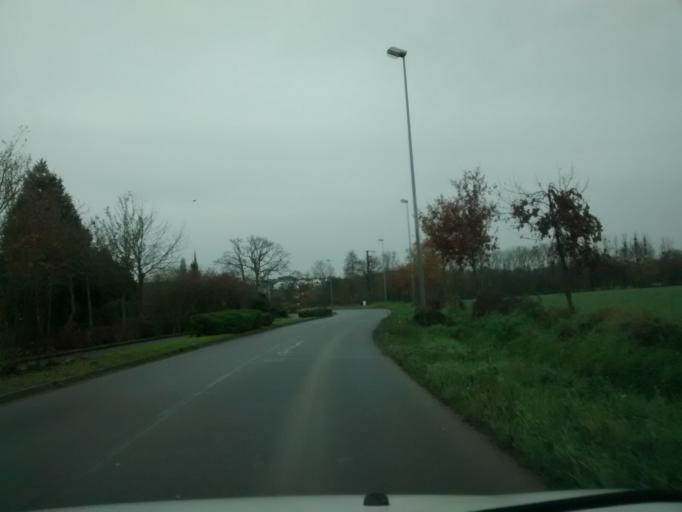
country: FR
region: Brittany
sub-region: Departement d'Ille-et-Vilaine
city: Acigne
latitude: 48.1274
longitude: -1.5328
